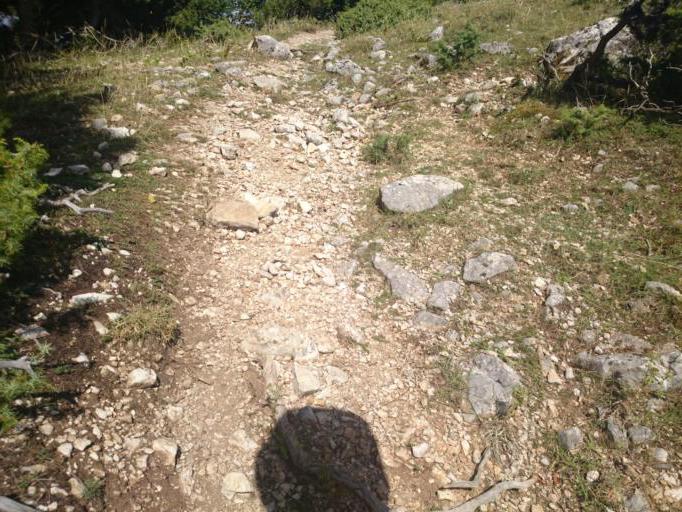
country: AL
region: Elbasan
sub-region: Rrethi i Gramshit
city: Kushove
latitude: 40.7336
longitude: 20.1437
